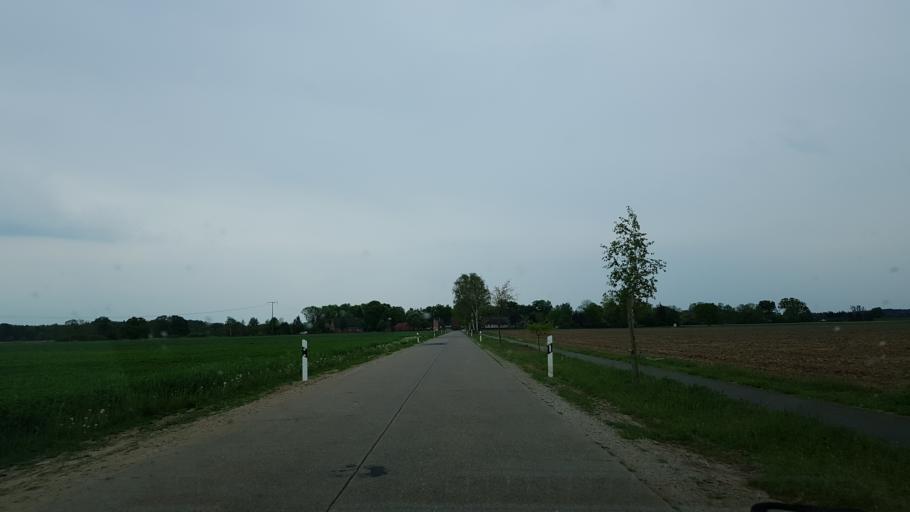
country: DE
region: Lower Saxony
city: Gartow
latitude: 53.0471
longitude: 11.4407
